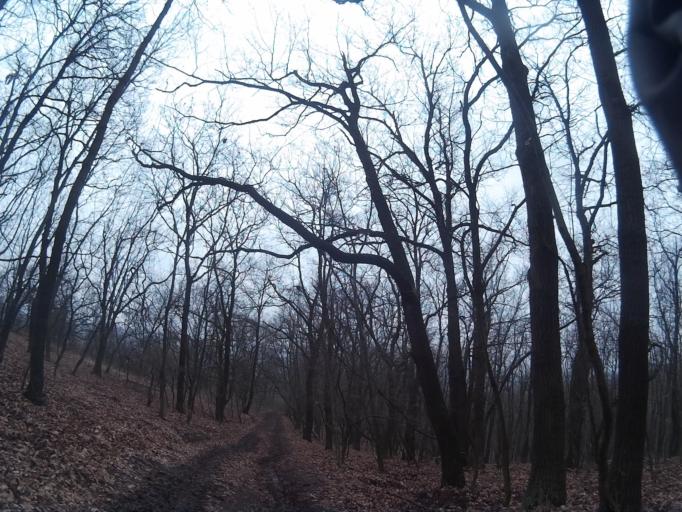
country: HU
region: Komarom-Esztergom
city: Tarjan
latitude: 47.5715
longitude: 18.5432
